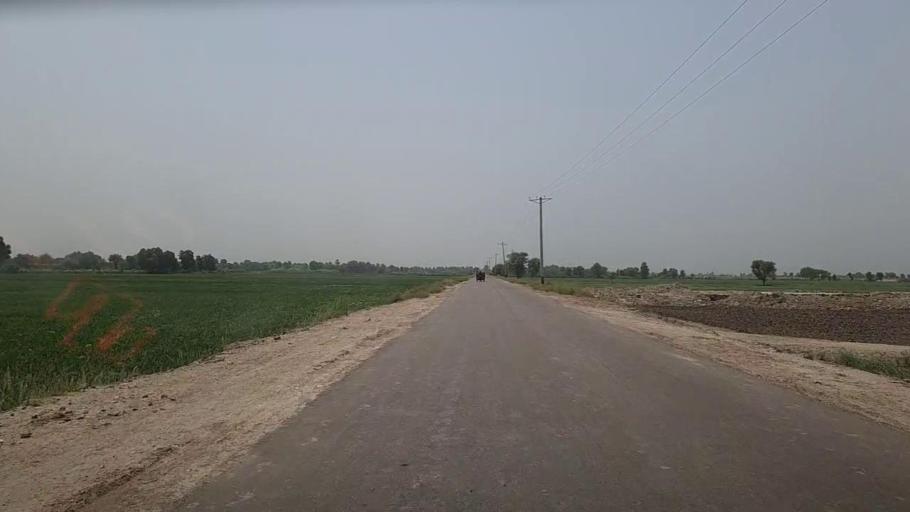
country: PK
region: Sindh
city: Sita Road
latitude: 27.0513
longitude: 67.9020
